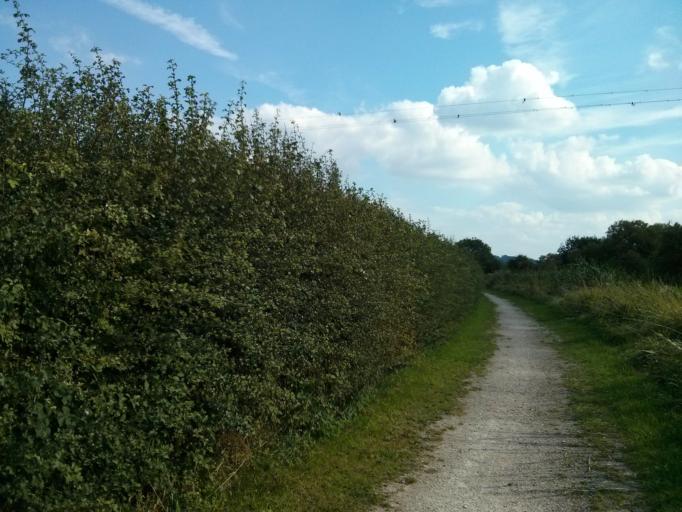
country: GB
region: England
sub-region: Lincolnshire
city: Long Bennington
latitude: 52.9117
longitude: -0.8245
